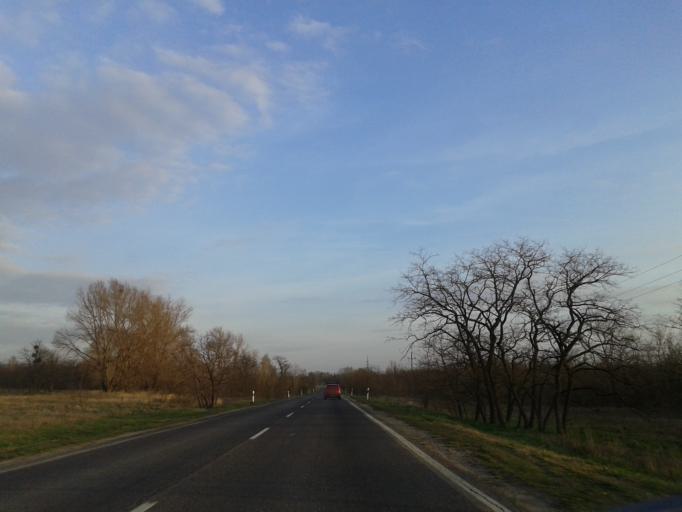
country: HU
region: Komarom-Esztergom
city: Szomod
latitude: 47.6825
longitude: 18.3146
